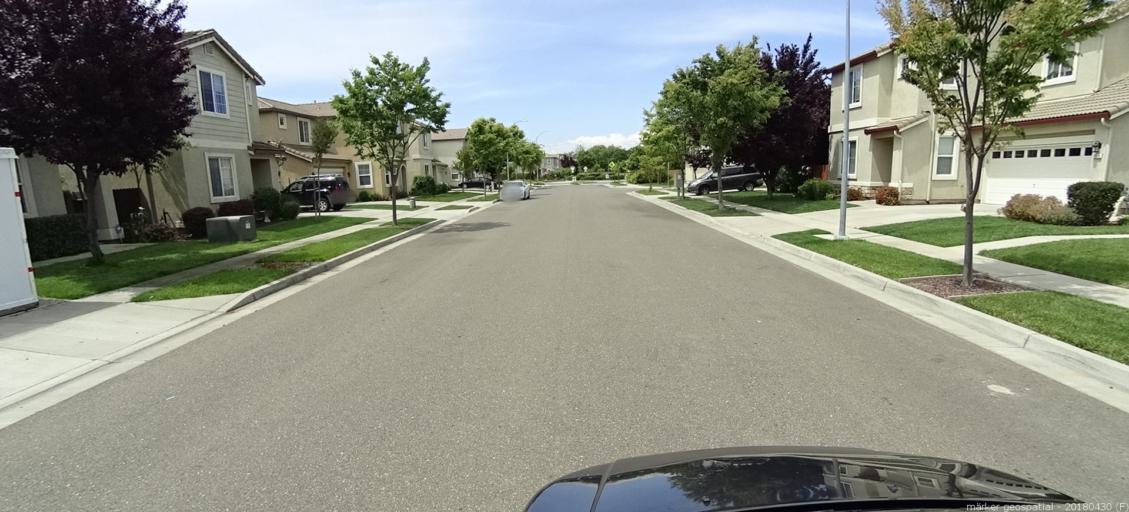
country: US
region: California
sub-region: Yolo County
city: West Sacramento
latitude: 38.5451
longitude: -121.5337
